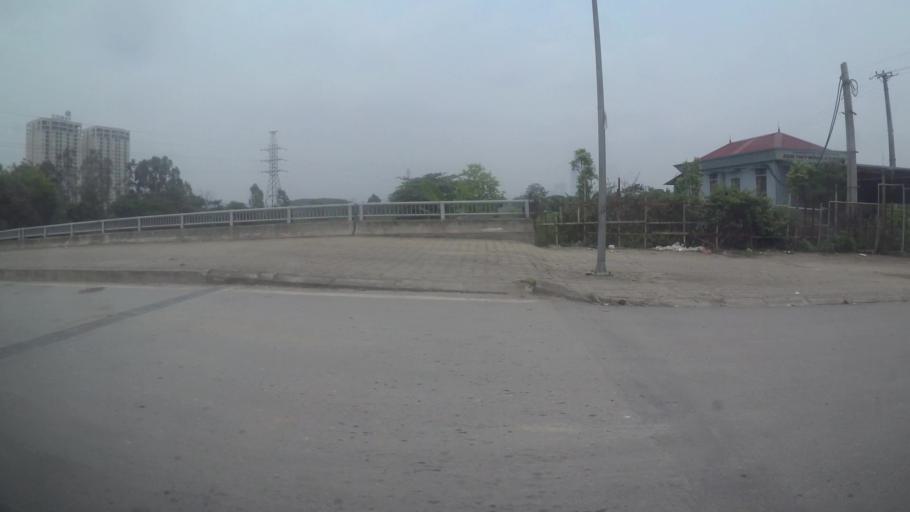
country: VN
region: Ha Noi
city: Cau Dien
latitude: 21.0128
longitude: 105.7465
